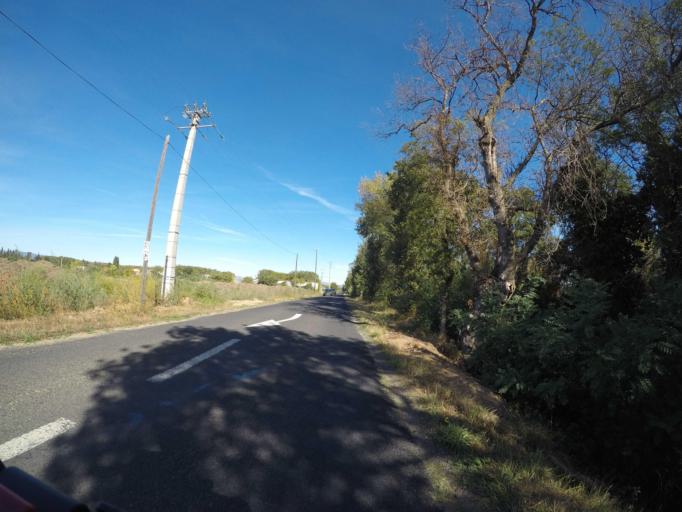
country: FR
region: Languedoc-Roussillon
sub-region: Departement des Pyrenees-Orientales
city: Le Soler
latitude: 42.6577
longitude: 2.7974
